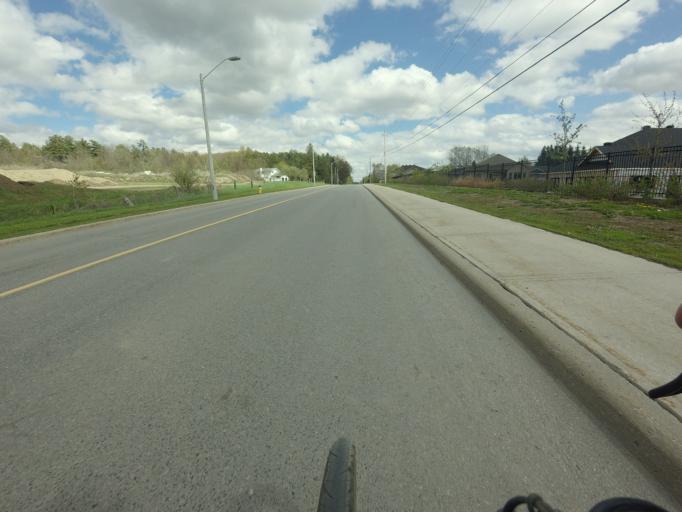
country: CA
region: Ontario
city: Bells Corners
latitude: 45.3447
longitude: -76.0220
